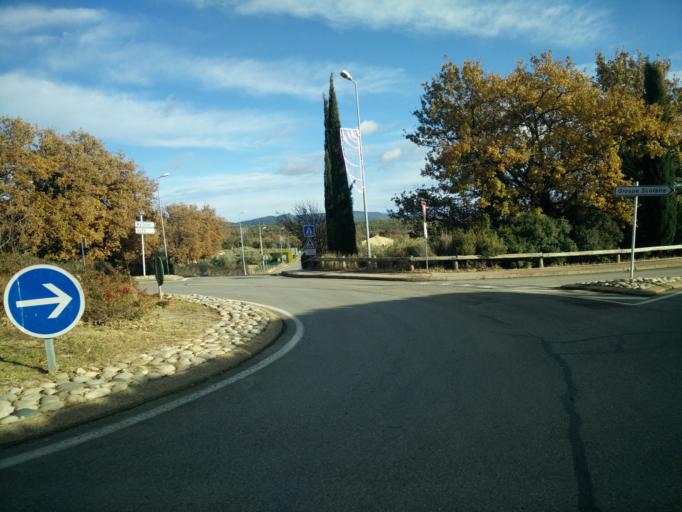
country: FR
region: Provence-Alpes-Cote d'Azur
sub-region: Departement du Var
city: Regusse
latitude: 43.6583
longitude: 6.1304
